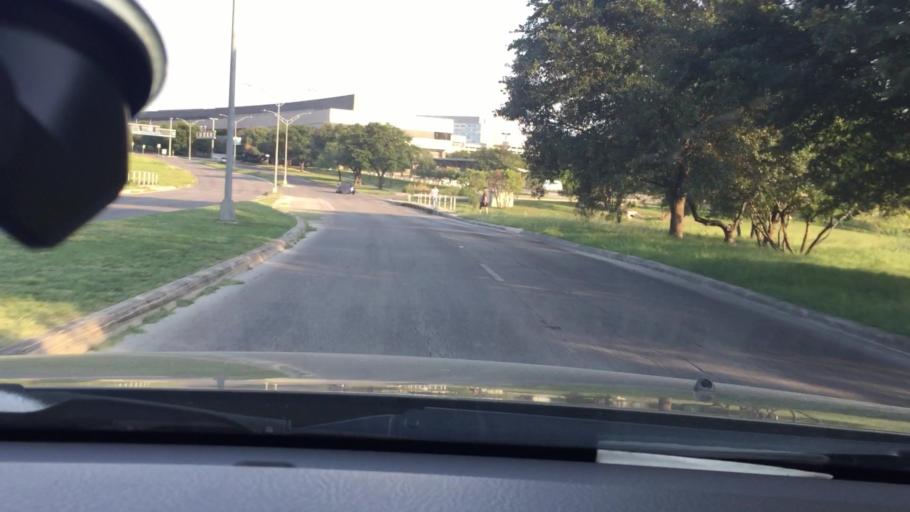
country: US
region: Texas
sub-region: Bexar County
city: Leon Valley
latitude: 29.5164
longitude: -98.5854
